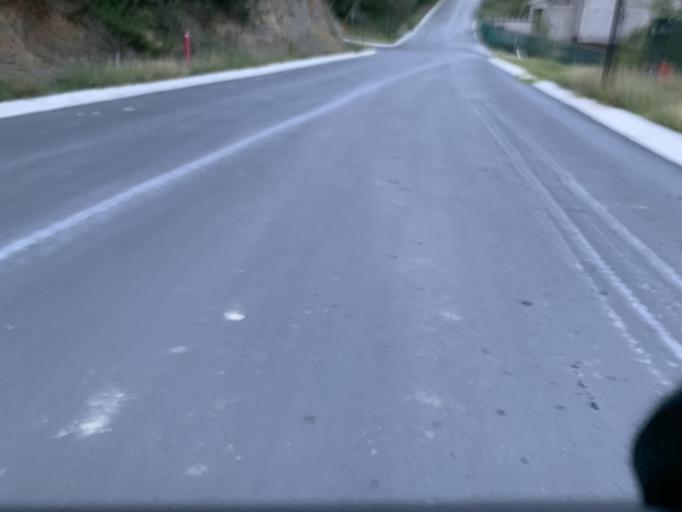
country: MX
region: Nuevo Leon
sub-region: Juarez
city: Bosques de San Pedro
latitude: 25.5251
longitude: -100.1928
